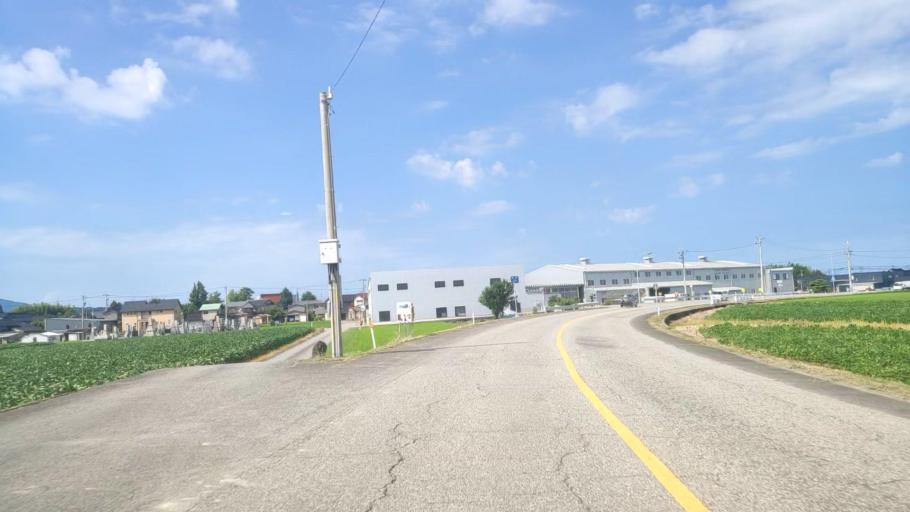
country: JP
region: Ishikawa
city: Tsurugi-asahimachi
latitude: 36.4658
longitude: 136.5908
